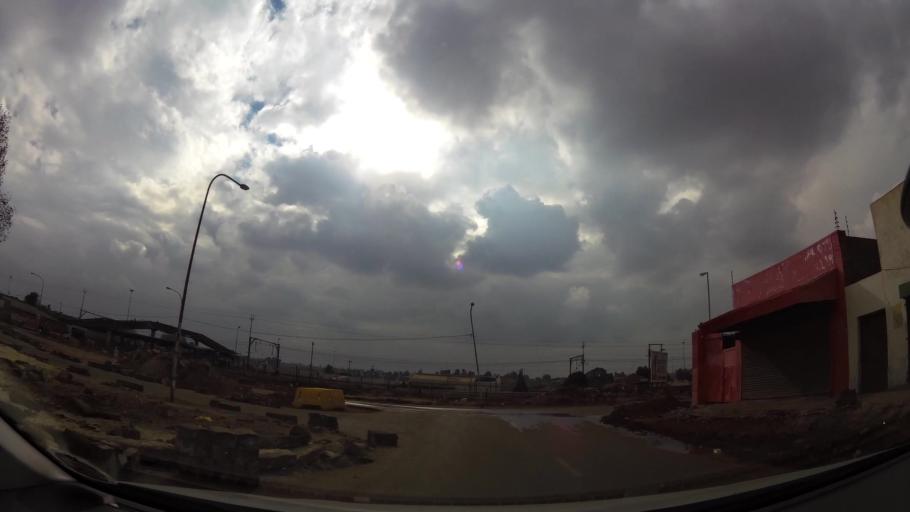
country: ZA
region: Gauteng
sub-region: City of Johannesburg Metropolitan Municipality
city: Soweto
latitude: -26.2624
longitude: 27.8481
